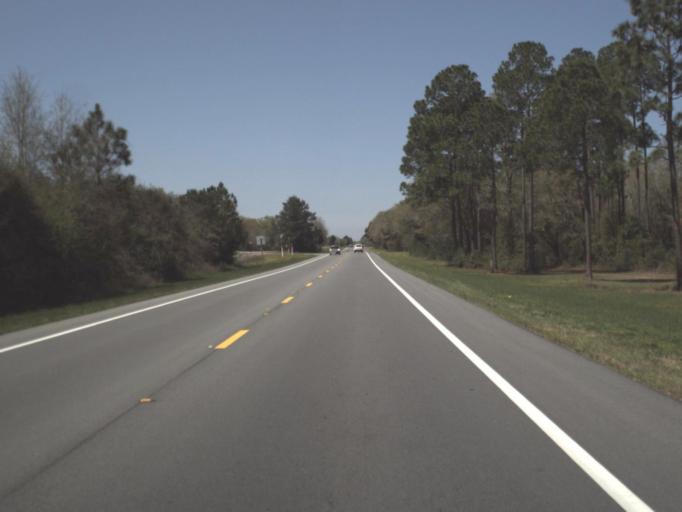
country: US
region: Florida
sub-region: Walton County
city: DeFuniak Springs
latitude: 30.7398
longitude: -86.1806
